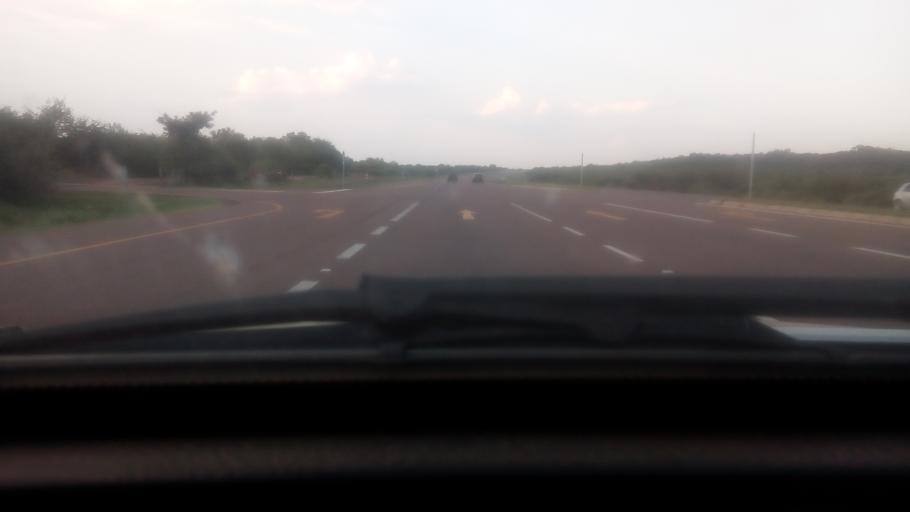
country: BW
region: Kgatleng
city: Bokaa
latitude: -24.4260
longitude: 26.0472
